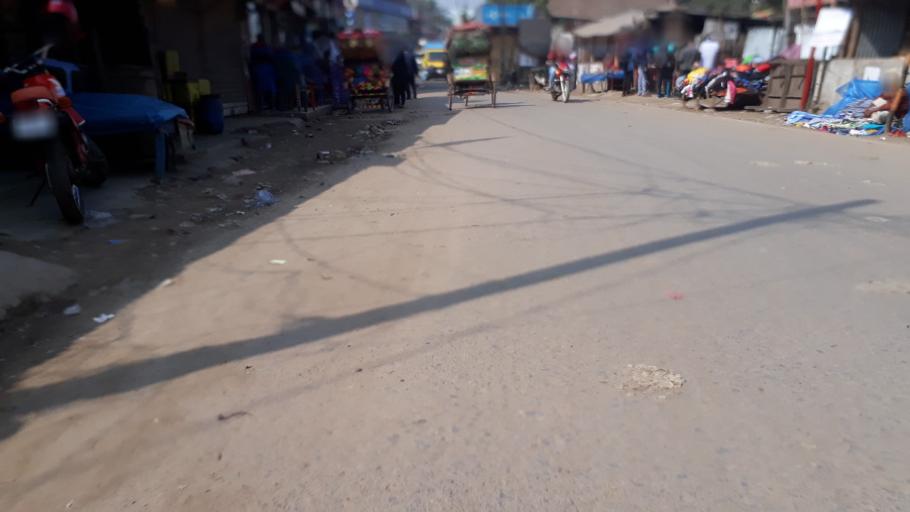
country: BD
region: Dhaka
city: Tungi
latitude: 23.8966
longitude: 90.3318
